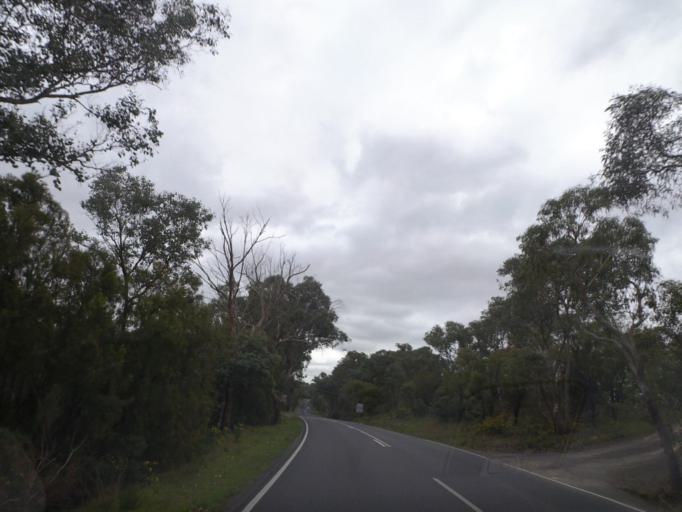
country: AU
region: Victoria
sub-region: Nillumbik
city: Diamond Creek
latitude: -37.6637
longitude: 145.1449
